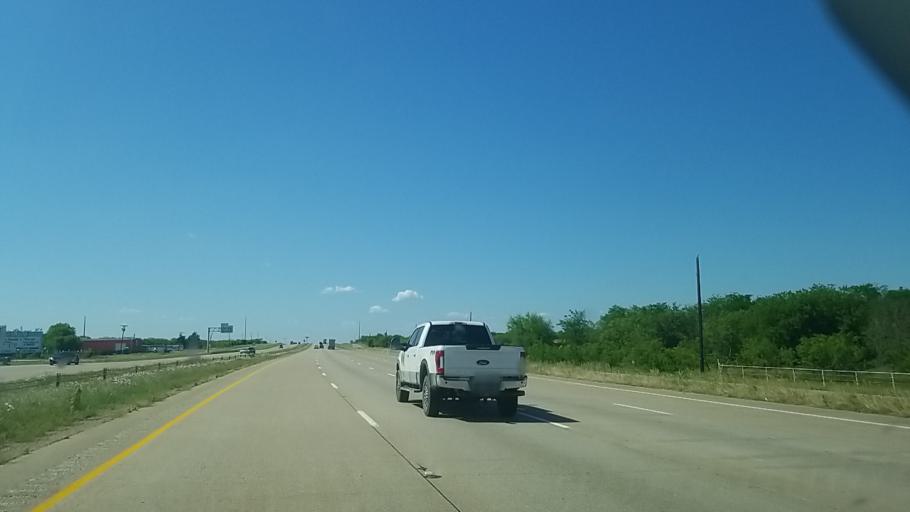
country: US
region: Texas
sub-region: Ellis County
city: Ennis
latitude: 32.3784
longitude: -96.6471
